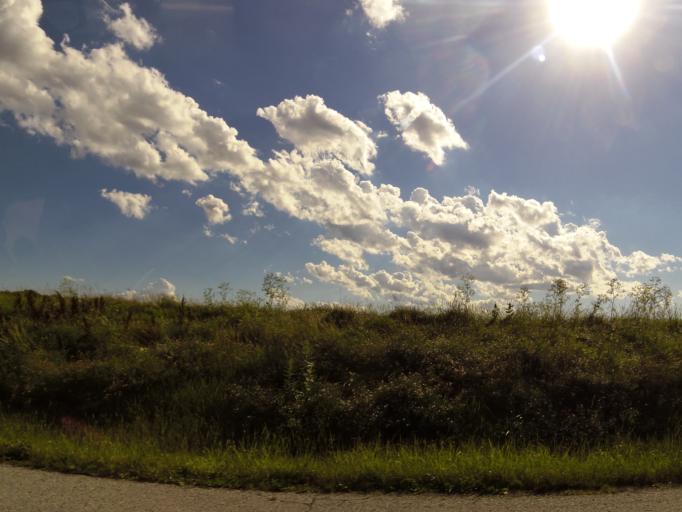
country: US
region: Missouri
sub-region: Marion County
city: Palmyra
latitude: 39.8345
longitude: -91.5188
